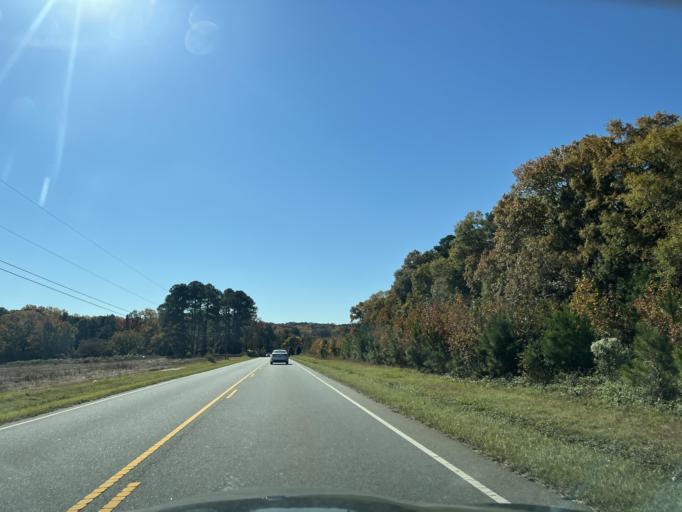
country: US
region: North Carolina
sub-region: Wake County
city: Fuquay-Varina
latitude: 35.6416
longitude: -78.7247
